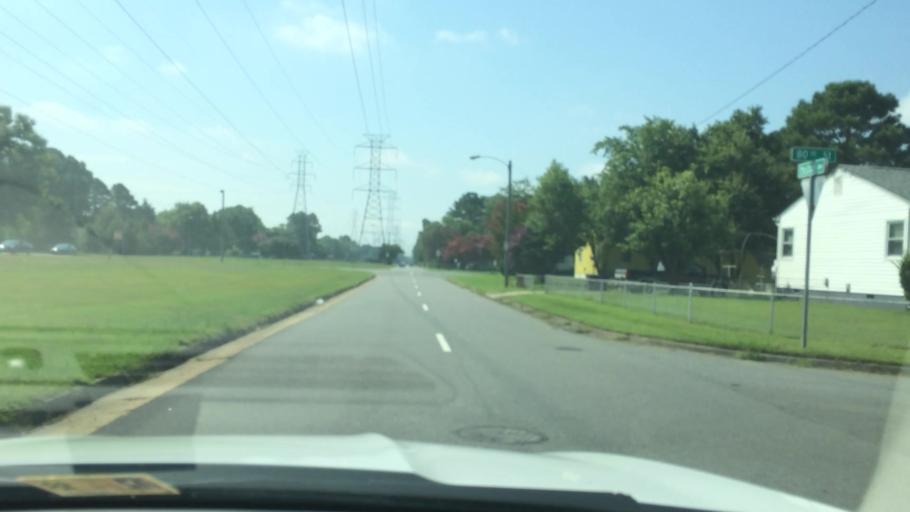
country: US
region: Virginia
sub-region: City of Newport News
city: Newport News
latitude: 37.0236
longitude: -76.4283
